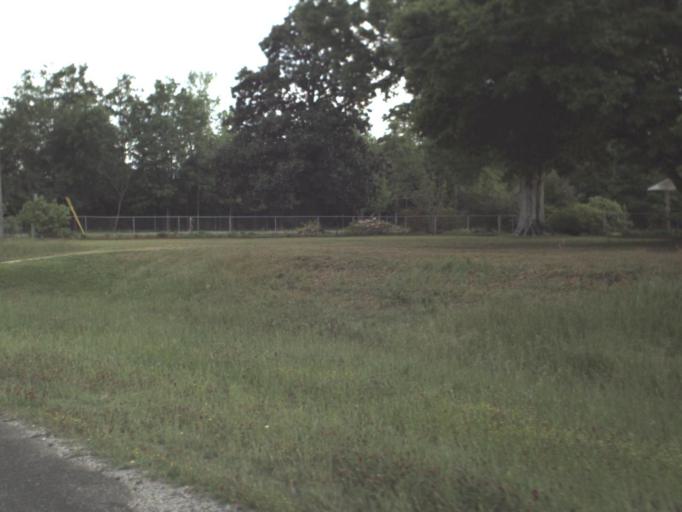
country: US
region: Florida
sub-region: Escambia County
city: Molino
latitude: 30.7126
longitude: -87.3501
